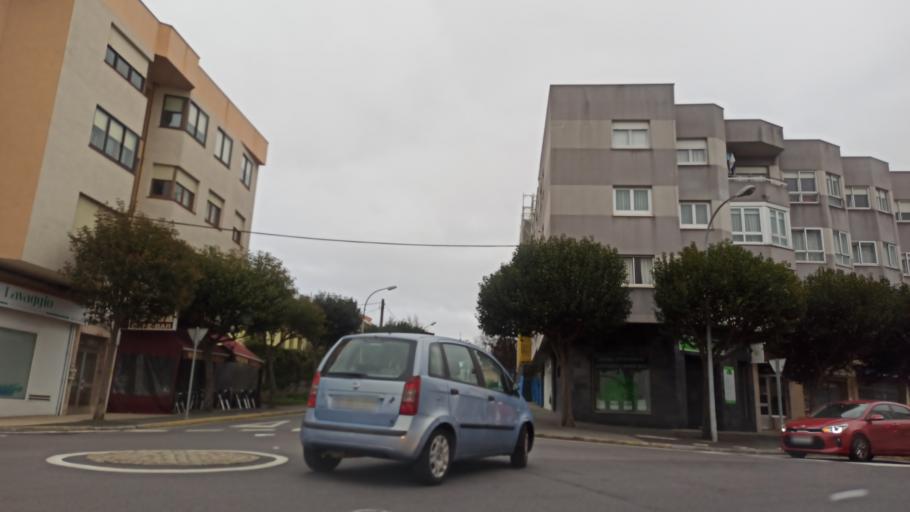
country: ES
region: Galicia
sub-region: Provincia da Coruna
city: Cambre
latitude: 43.3329
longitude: -8.3715
